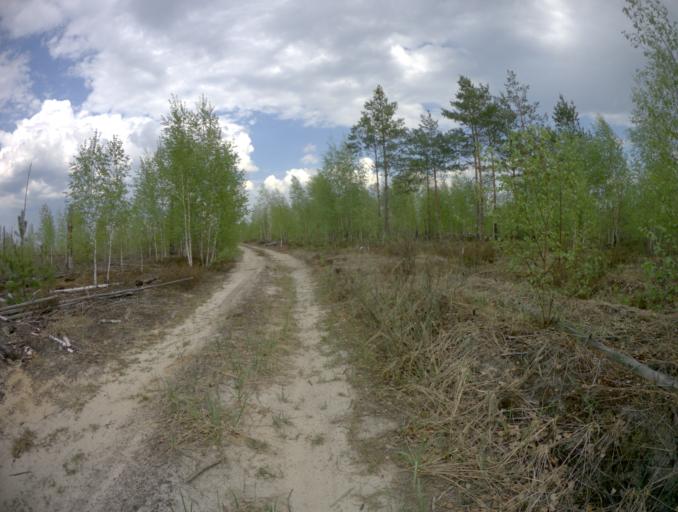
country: RU
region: Ivanovo
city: Talitsy
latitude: 56.4464
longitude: 42.2344
